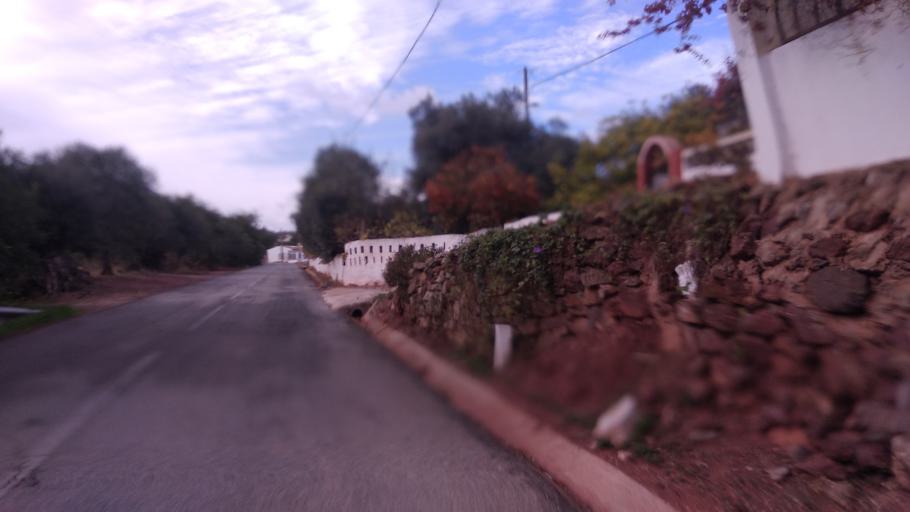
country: PT
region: Faro
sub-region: Sao Bras de Alportel
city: Sao Bras de Alportel
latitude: 37.1749
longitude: -7.8991
